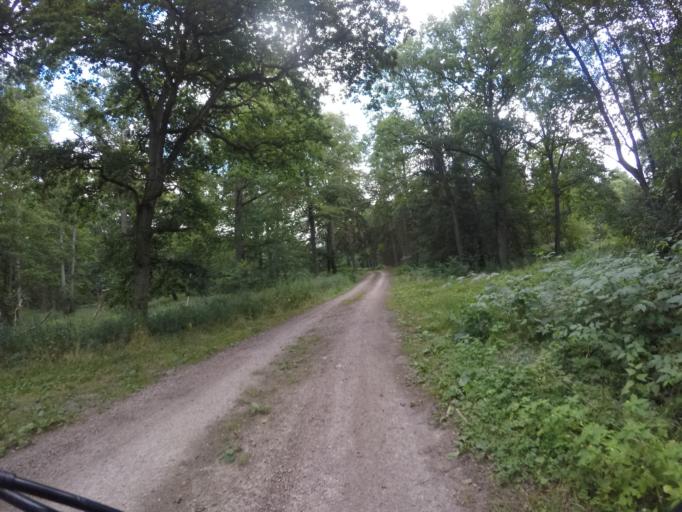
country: DE
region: Mecklenburg-Vorpommern
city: Lubtheen
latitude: 53.2815
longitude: 10.9815
